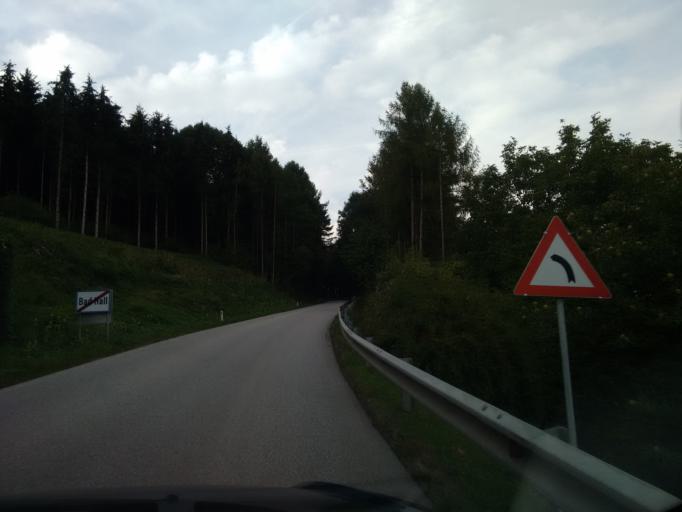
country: AT
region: Upper Austria
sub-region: Politischer Bezirk Steyr-Land
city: Pfarrkirchen bei Bad Hall
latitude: 48.0403
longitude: 14.1975
